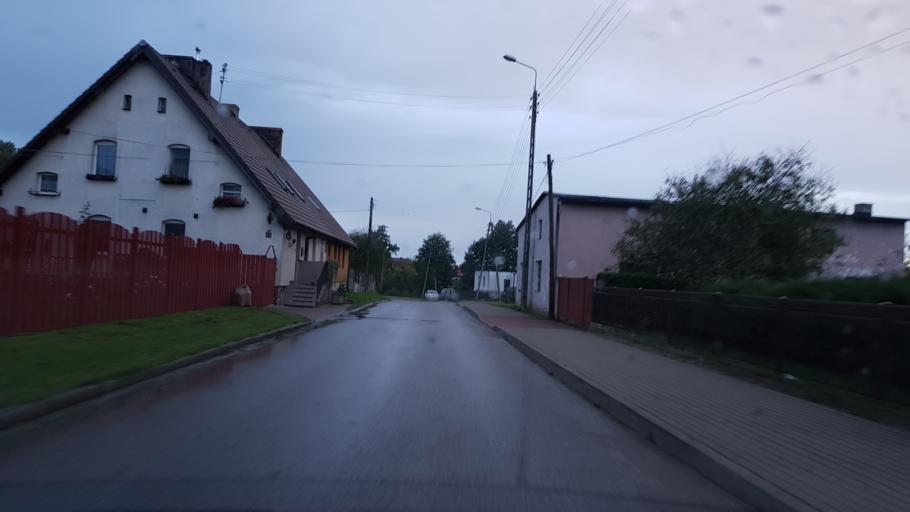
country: PL
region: Greater Poland Voivodeship
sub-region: Powiat zlotowski
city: Krajenka
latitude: 53.2981
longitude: 16.9849
